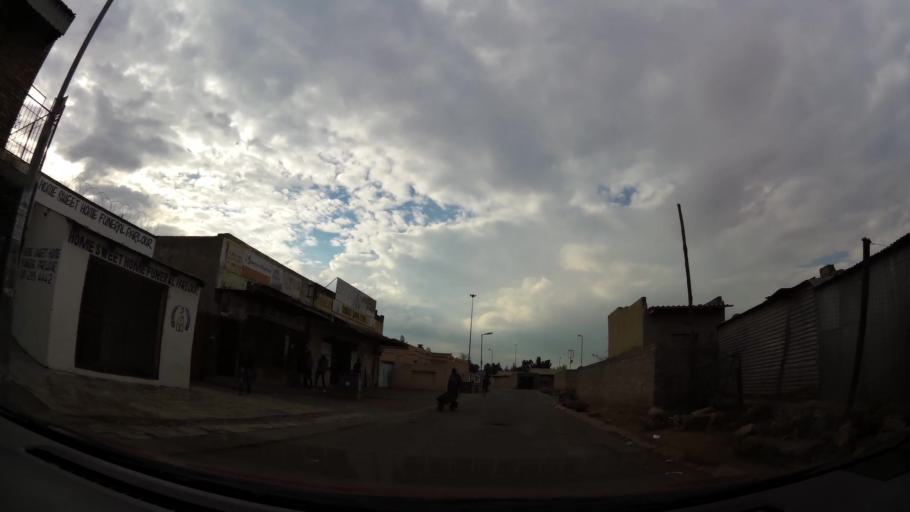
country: ZA
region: Gauteng
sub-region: City of Johannesburg Metropolitan Municipality
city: Soweto
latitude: -26.2508
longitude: 27.8241
